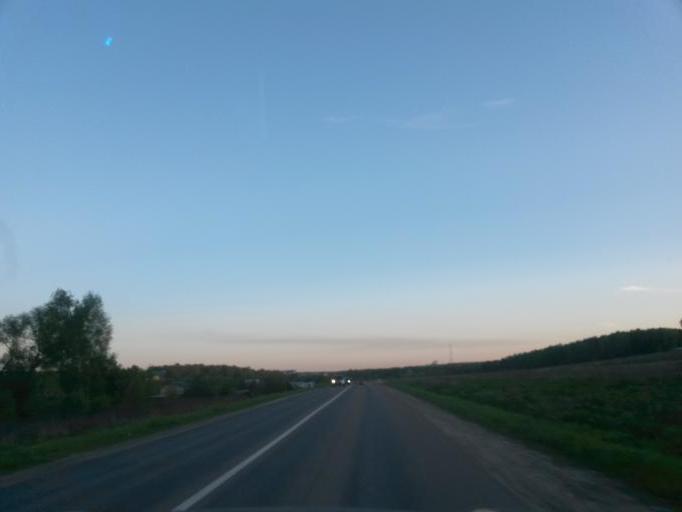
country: RU
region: Moskovskaya
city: Lyubuchany
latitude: 55.2902
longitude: 37.6269
